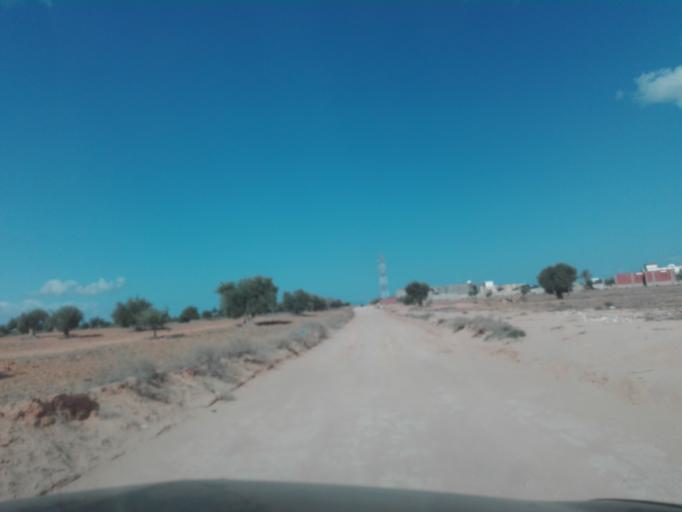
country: TN
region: Madanin
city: Bin Qirdan
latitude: 33.1648
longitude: 11.1960
